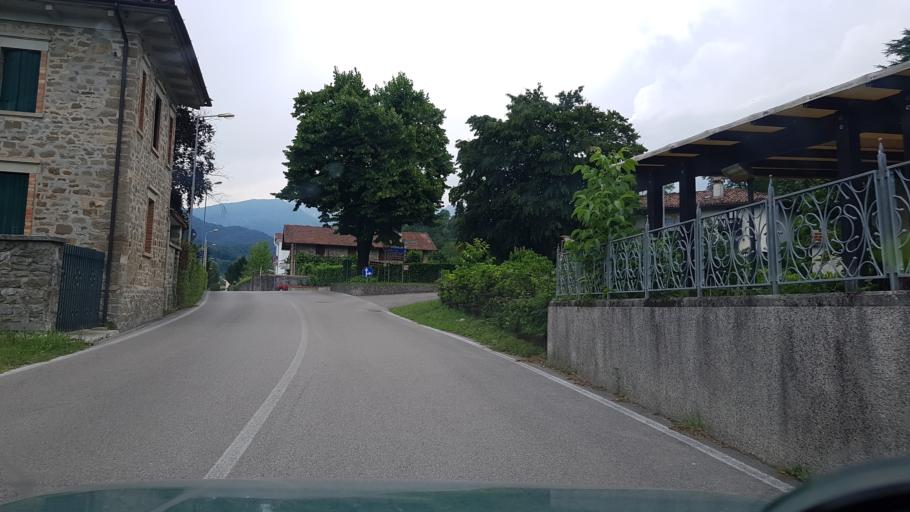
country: IT
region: Friuli Venezia Giulia
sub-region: Provincia di Udine
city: Tarcento
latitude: 46.2144
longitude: 13.2269
